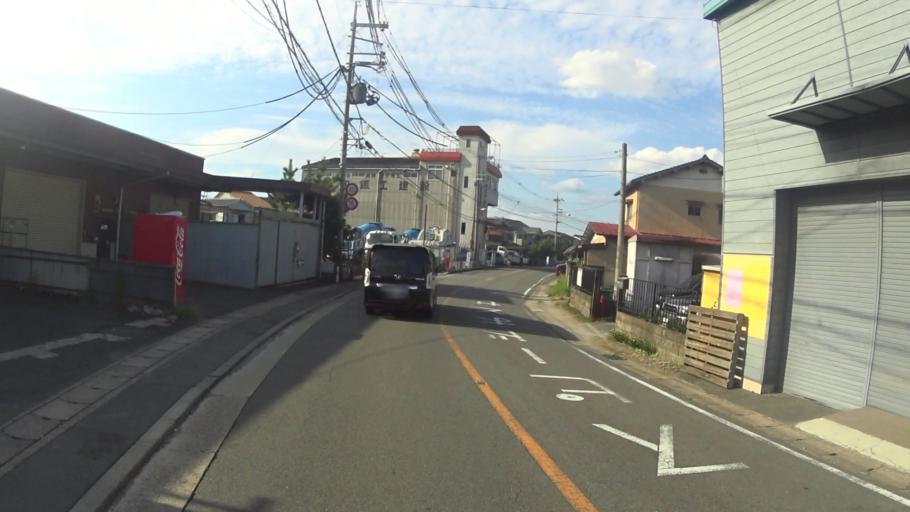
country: JP
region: Kyoto
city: Muko
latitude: 34.9196
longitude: 135.7224
